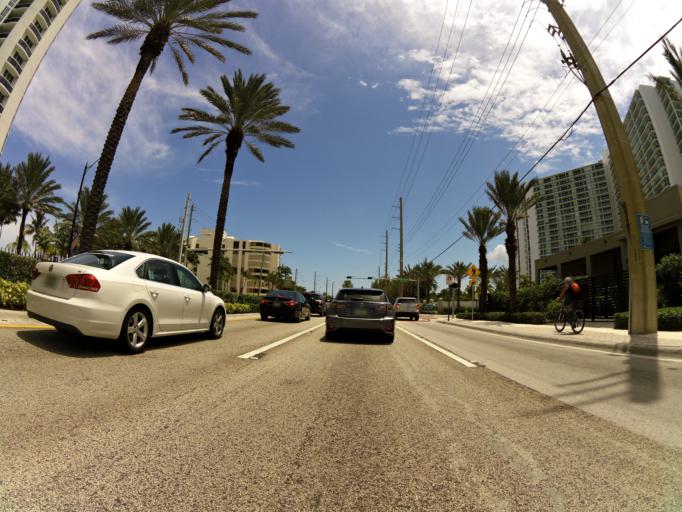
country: US
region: Florida
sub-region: Miami-Dade County
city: Sunny Isles Beach
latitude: 25.9229
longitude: -80.1225
